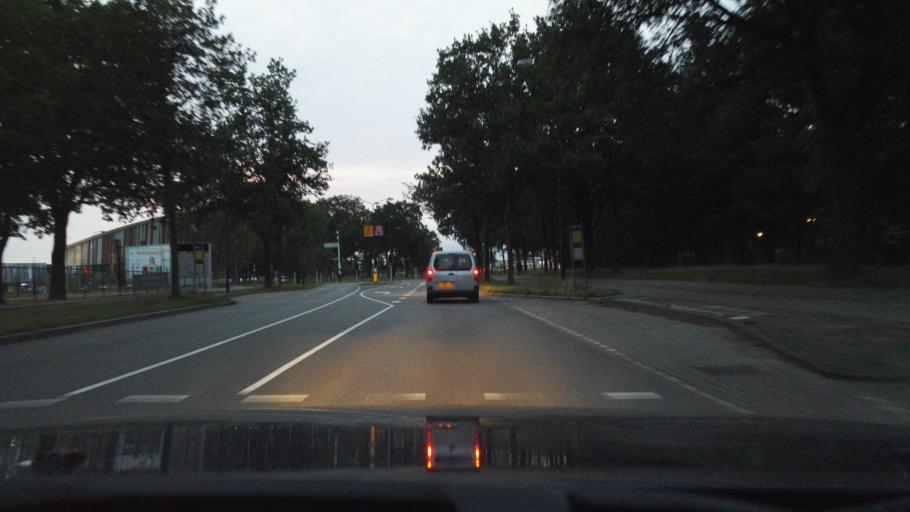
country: NL
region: Gelderland
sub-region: Gemeente Apeldoorn
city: Apeldoorn
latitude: 52.2071
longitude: 5.9995
